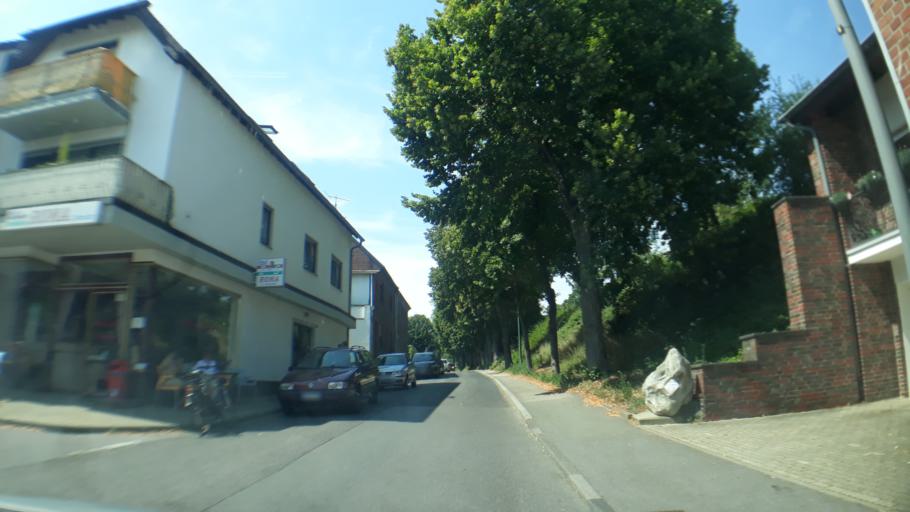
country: DE
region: North Rhine-Westphalia
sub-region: Regierungsbezirk Koln
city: Langerwehe
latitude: 50.8391
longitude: 6.3429
